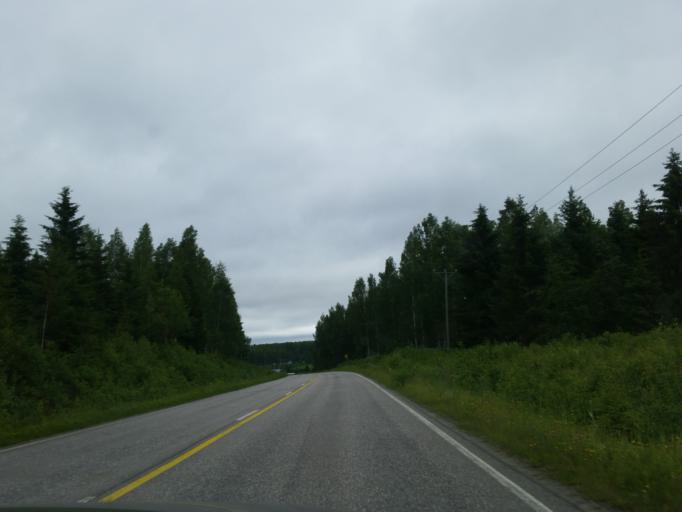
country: FI
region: Northern Savo
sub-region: Koillis-Savo
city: Kaavi
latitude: 62.9720
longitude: 28.5064
